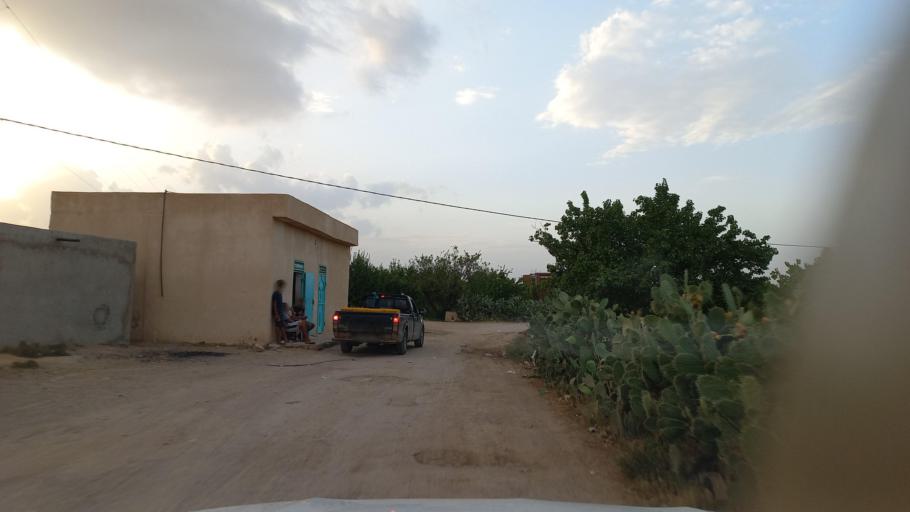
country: TN
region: Al Qasrayn
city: Kasserine
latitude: 35.2725
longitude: 9.0540
